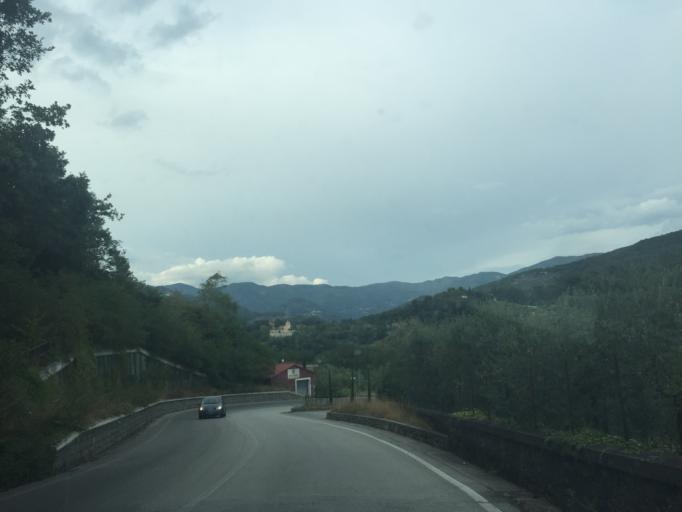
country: IT
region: Tuscany
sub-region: Provincia di Pistoia
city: Pistoia
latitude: 43.9730
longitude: 10.8872
